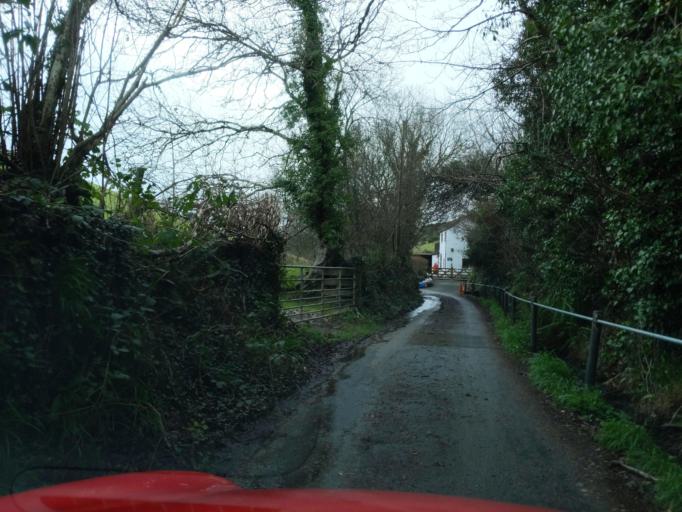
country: GB
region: England
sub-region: Cornwall
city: Duloe
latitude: 50.3504
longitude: -4.5138
